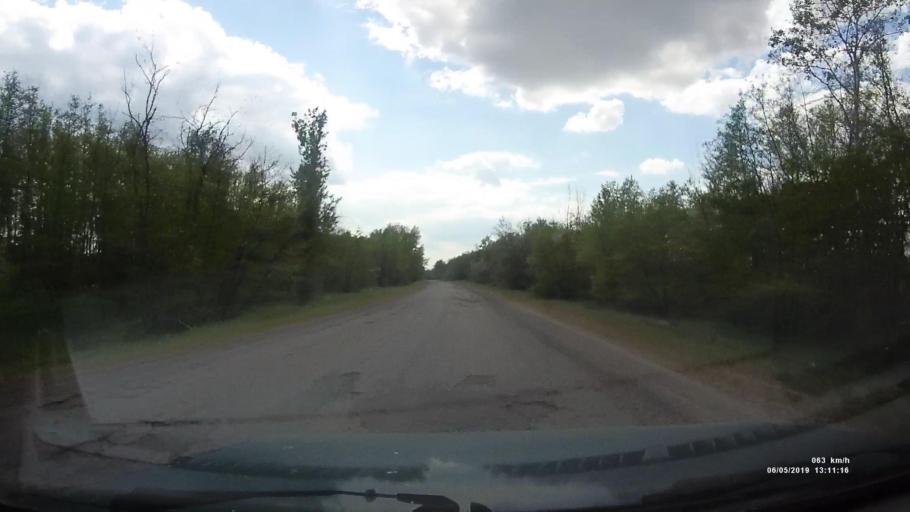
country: RU
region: Rostov
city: Ust'-Donetskiy
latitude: 47.7567
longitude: 40.9598
